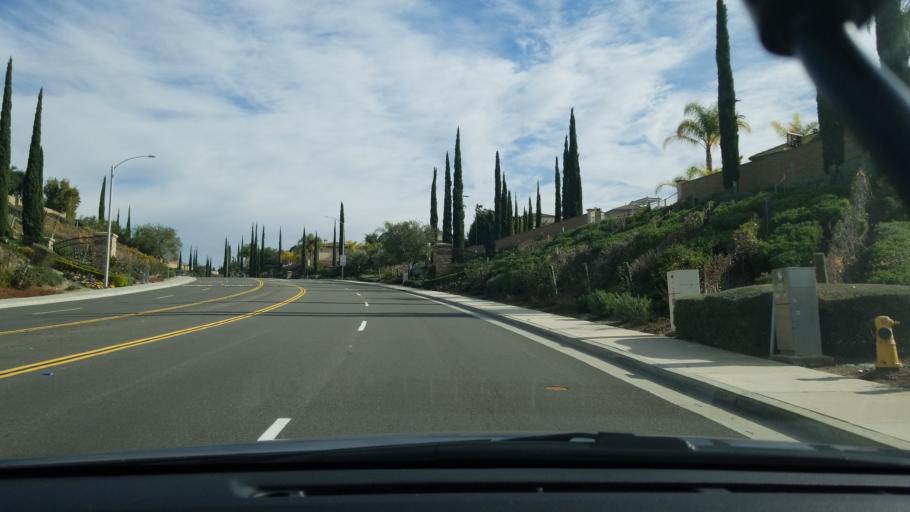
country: US
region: California
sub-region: Riverside County
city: Temecula
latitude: 33.4773
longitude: -117.0700
